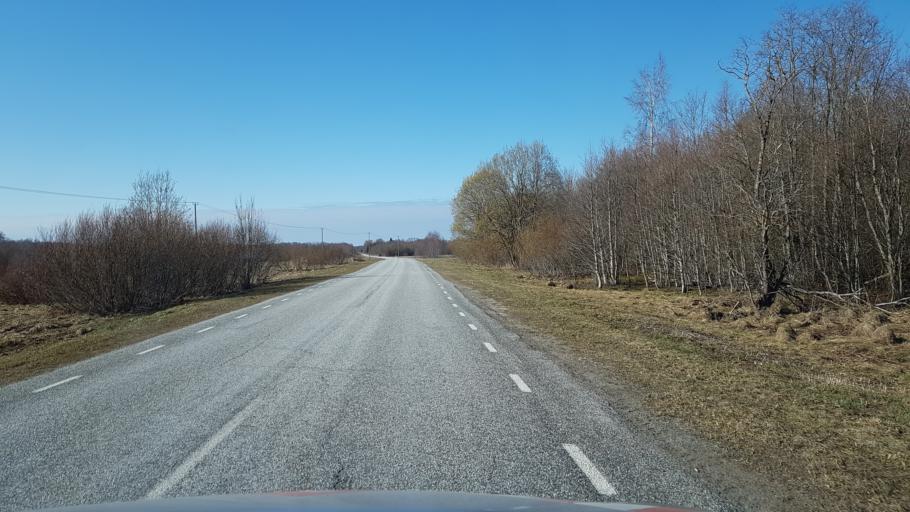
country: EE
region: Laeaene-Virumaa
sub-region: Haljala vald
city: Haljala
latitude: 59.4825
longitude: 26.1537
